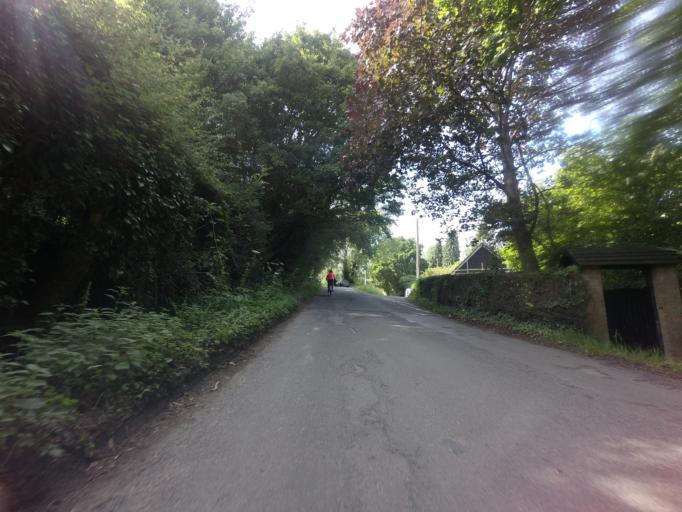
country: GB
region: England
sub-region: East Sussex
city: Rye
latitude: 50.9709
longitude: 0.7415
